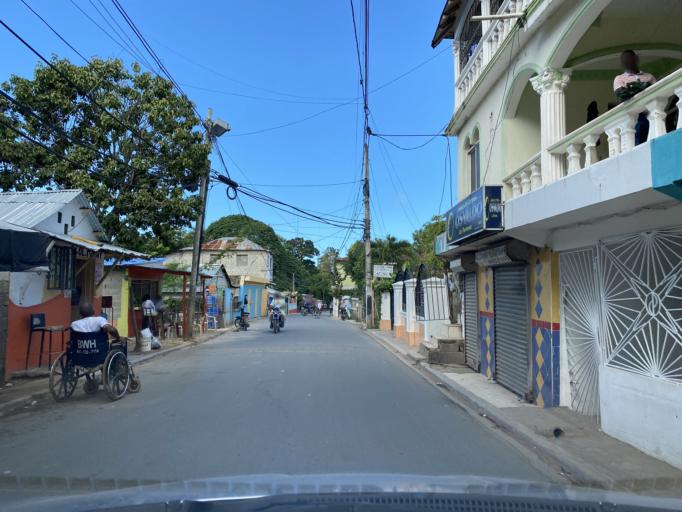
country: DO
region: Samana
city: Las Terrenas
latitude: 19.3073
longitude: -69.5413
